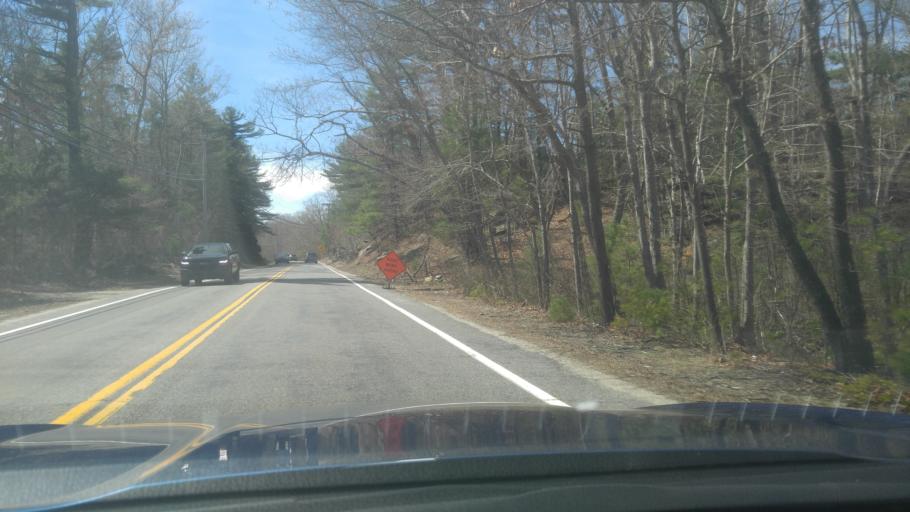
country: US
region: Rhode Island
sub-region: Washington County
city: Exeter
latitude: 41.5795
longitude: -71.5961
